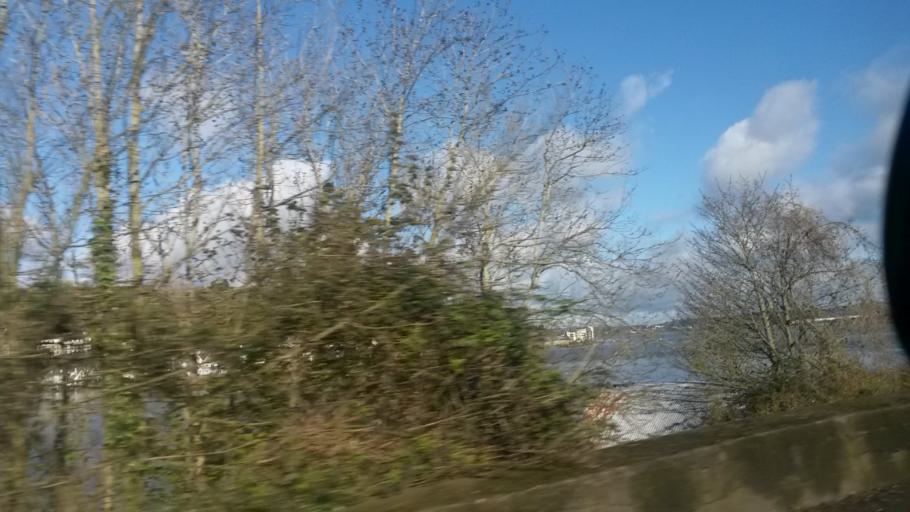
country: IE
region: Munster
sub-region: County Cork
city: Passage West
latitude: 51.8647
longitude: -8.3257
